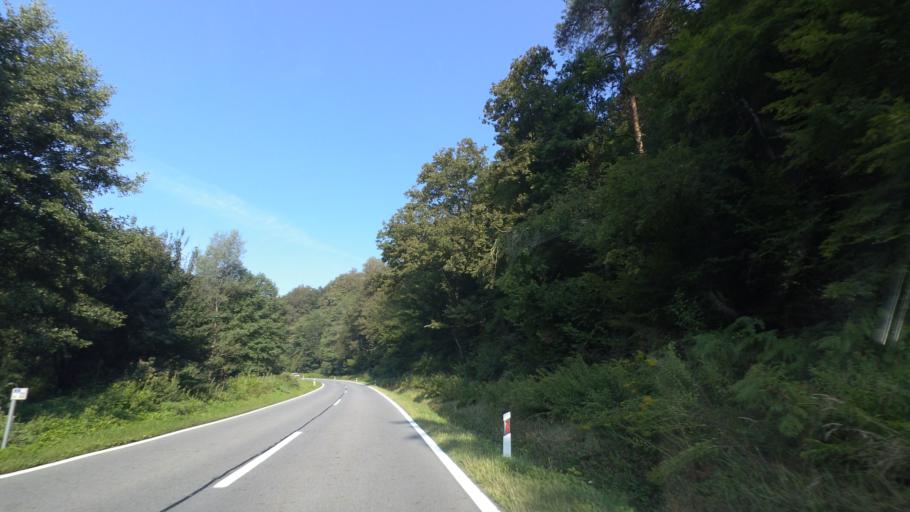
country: HR
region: Brodsko-Posavska
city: Cernik
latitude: 45.4574
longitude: 17.4423
